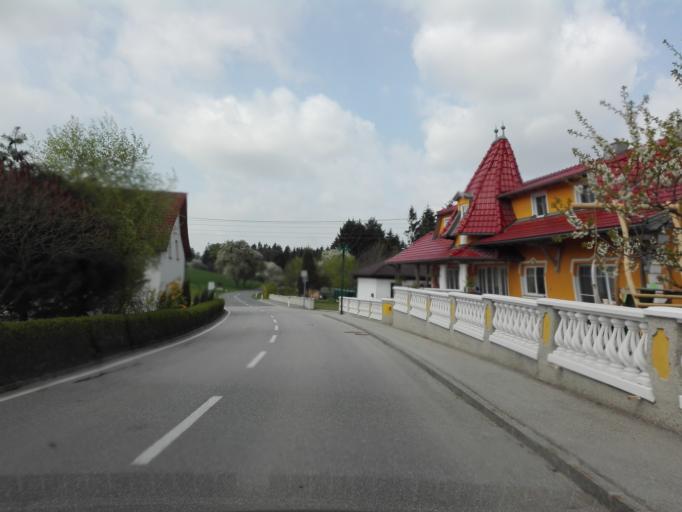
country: AT
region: Upper Austria
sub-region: Politischer Bezirk Perg
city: Perg
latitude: 48.2801
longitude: 14.6745
